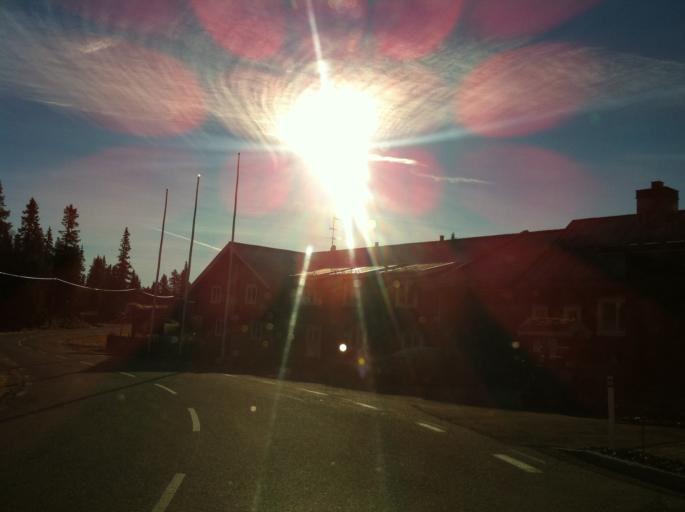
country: NO
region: Hedmark
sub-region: Engerdal
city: Engerdal
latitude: 62.0704
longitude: 12.3111
